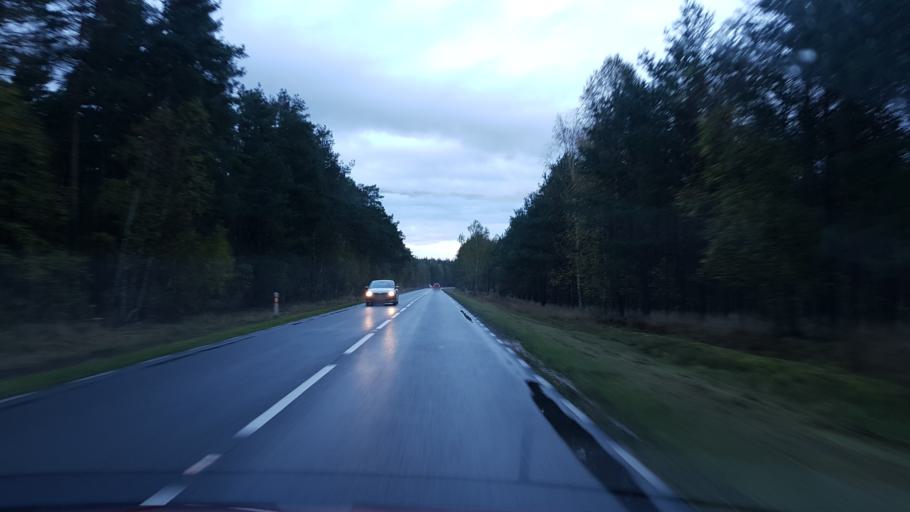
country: PL
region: Greater Poland Voivodeship
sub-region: Powiat pilski
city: Pila
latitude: 53.1954
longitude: 16.8260
